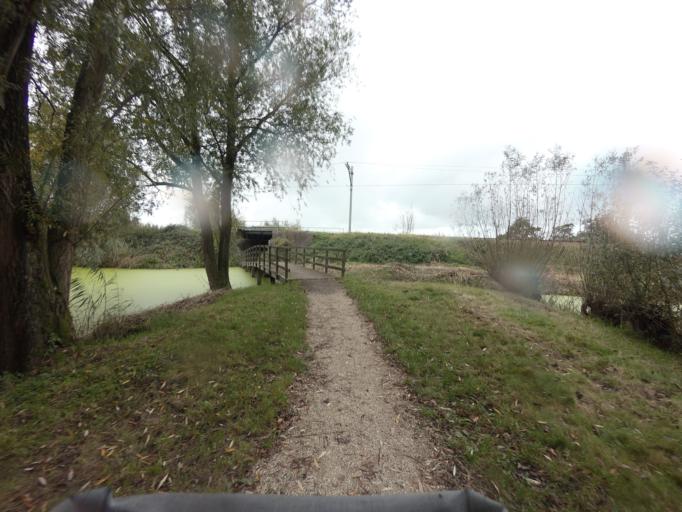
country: NL
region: South Holland
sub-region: Gemeente Boskoop
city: Boskoop
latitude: 52.0992
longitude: 4.6545
